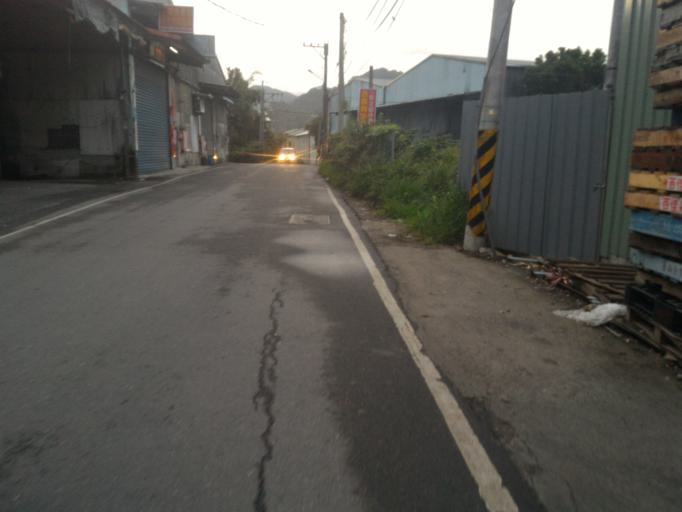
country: TW
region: Taipei
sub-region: Taipei
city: Banqiao
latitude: 24.9548
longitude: 121.4046
